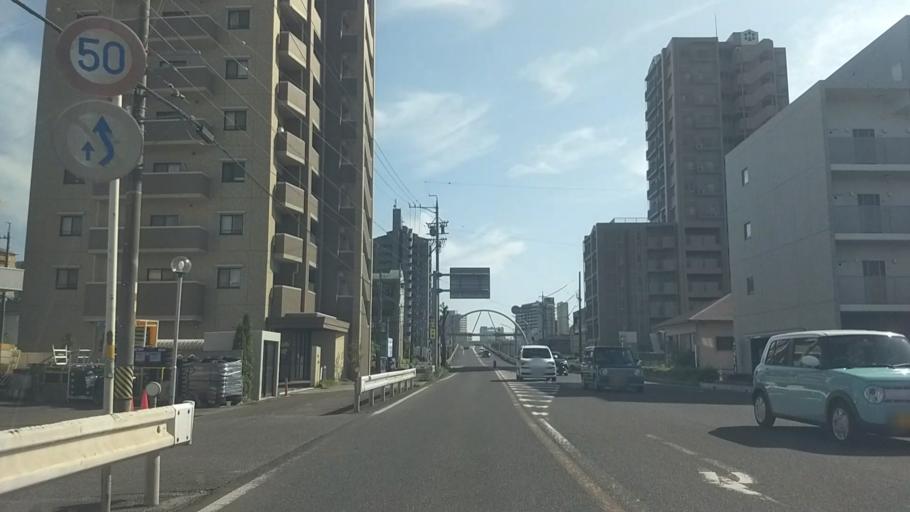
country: JP
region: Aichi
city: Anjo
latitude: 34.9734
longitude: 137.0629
